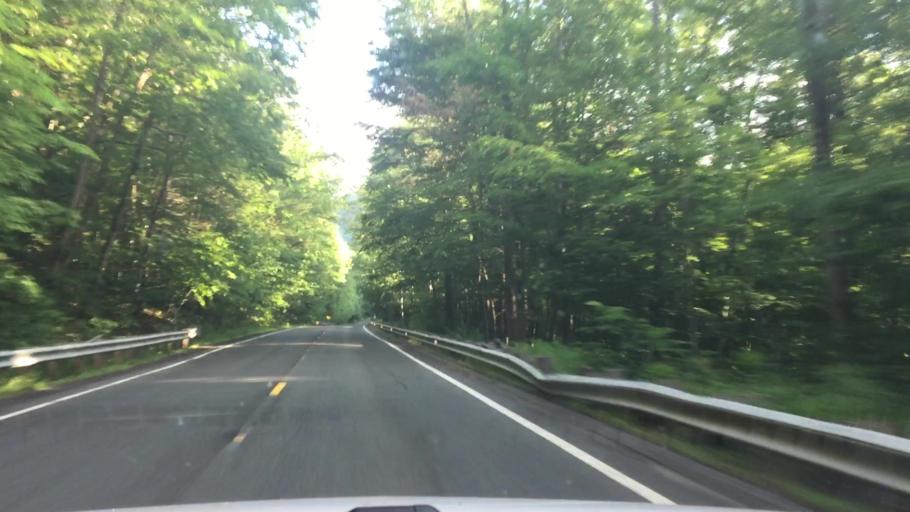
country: US
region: Massachusetts
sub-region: Hampshire County
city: Chesterfield
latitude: 42.3198
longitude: -72.8693
